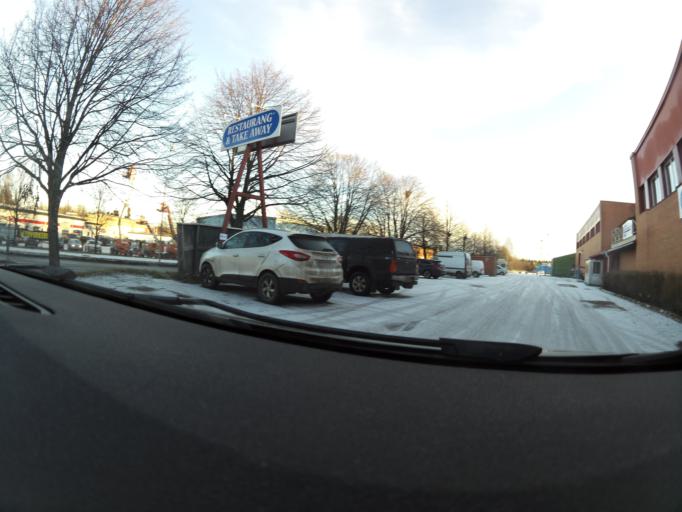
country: SE
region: Gaevleborg
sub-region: Gavle Kommun
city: Gavle
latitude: 60.6668
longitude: 17.1697
